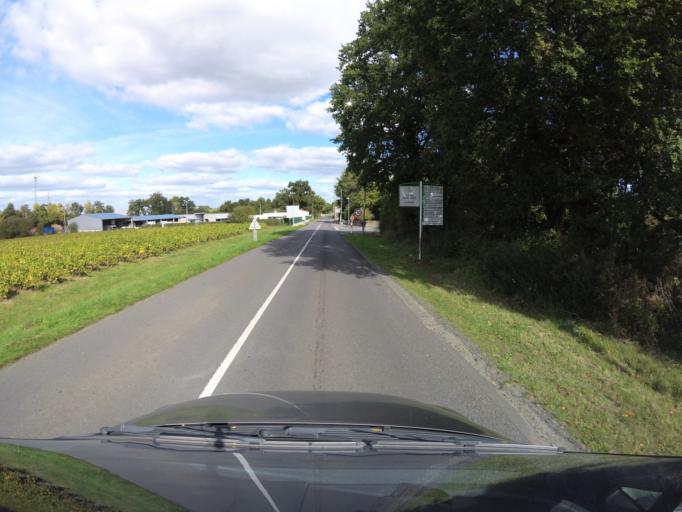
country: FR
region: Pays de la Loire
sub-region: Departement de la Loire-Atlantique
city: Monnieres
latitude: 47.1472
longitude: -1.3516
